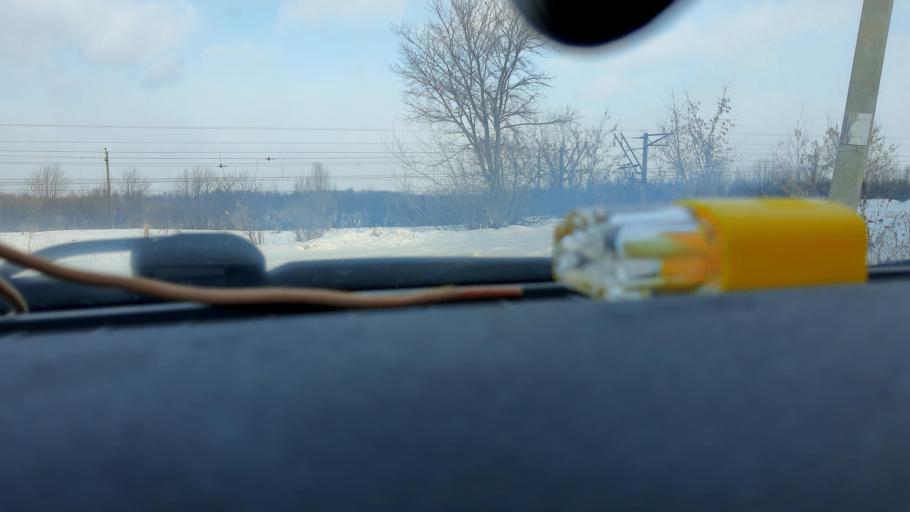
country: RU
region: Bashkortostan
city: Kabakovo
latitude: 54.6355
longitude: 56.0630
